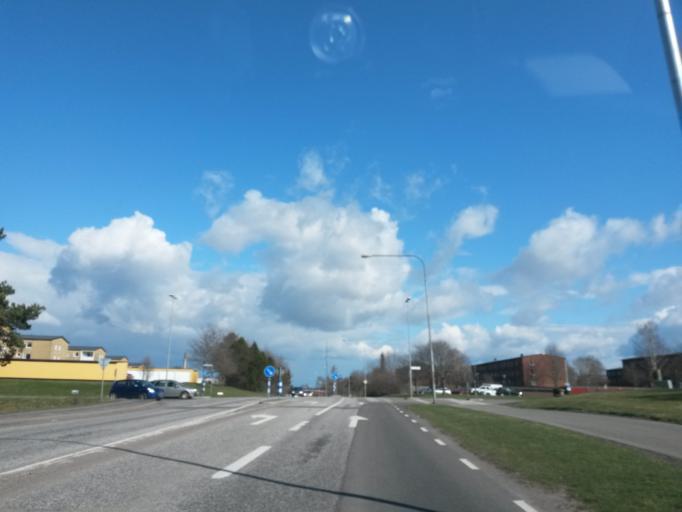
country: SE
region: Vaestra Goetaland
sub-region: Skovde Kommun
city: Skoevde
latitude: 58.4066
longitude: 13.8600
